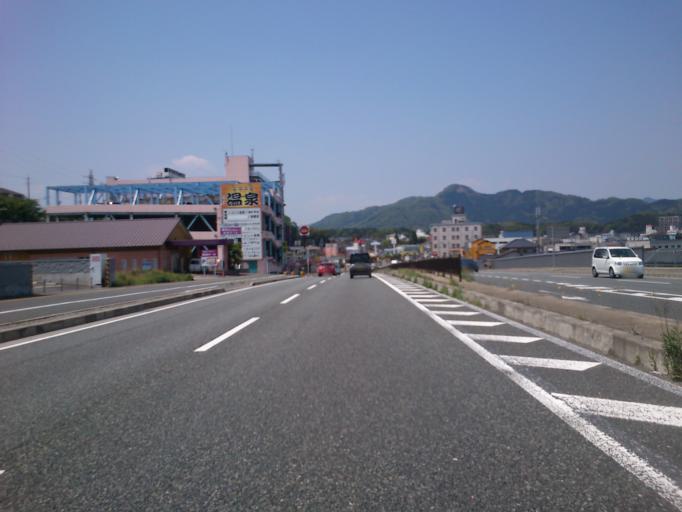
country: JP
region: Kyoto
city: Fukuchiyama
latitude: 35.2914
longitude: 135.1204
